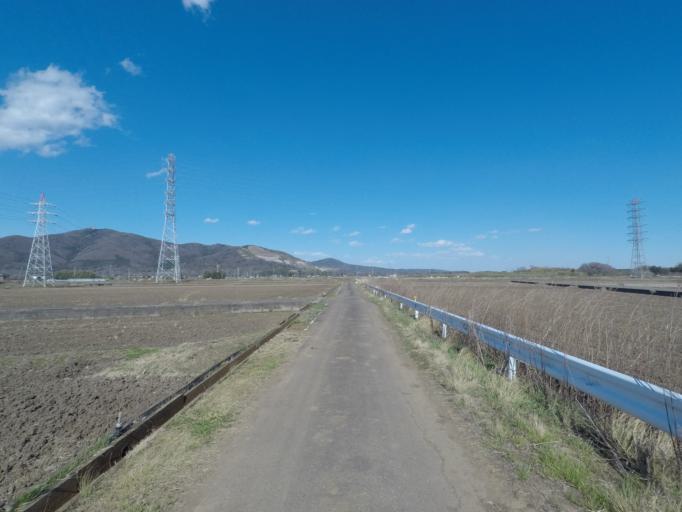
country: JP
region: Ibaraki
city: Tsukuba
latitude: 36.1361
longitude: 140.1161
